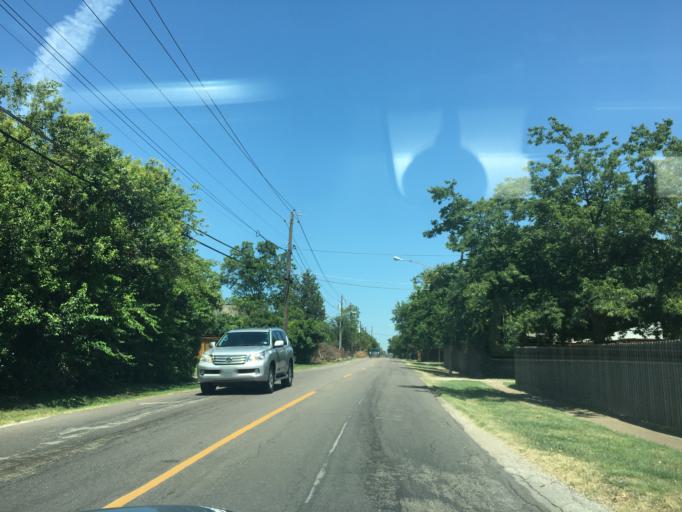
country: US
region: Texas
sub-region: Dallas County
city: Highland Park
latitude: 32.8480
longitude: -96.7434
